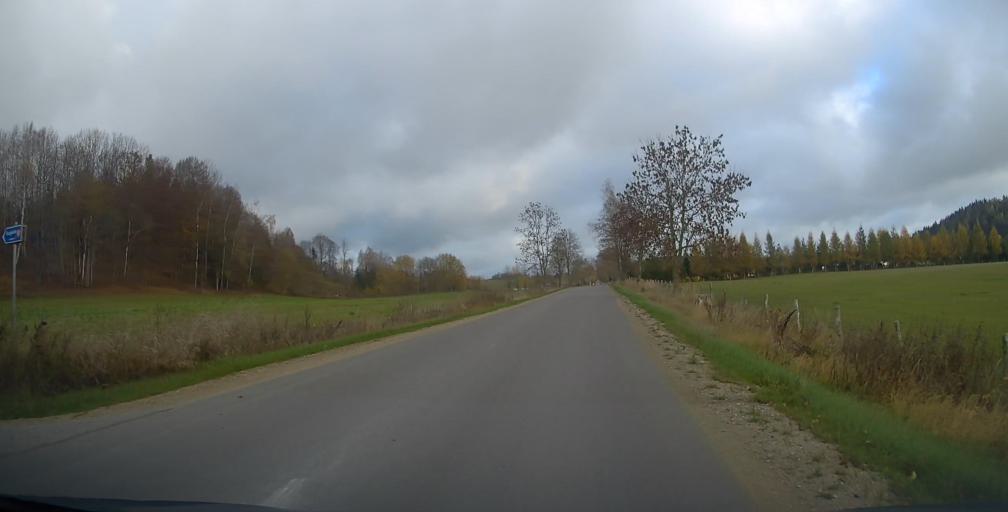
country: PL
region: Podlasie
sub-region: Suwalki
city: Suwalki
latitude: 54.2982
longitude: 22.8784
